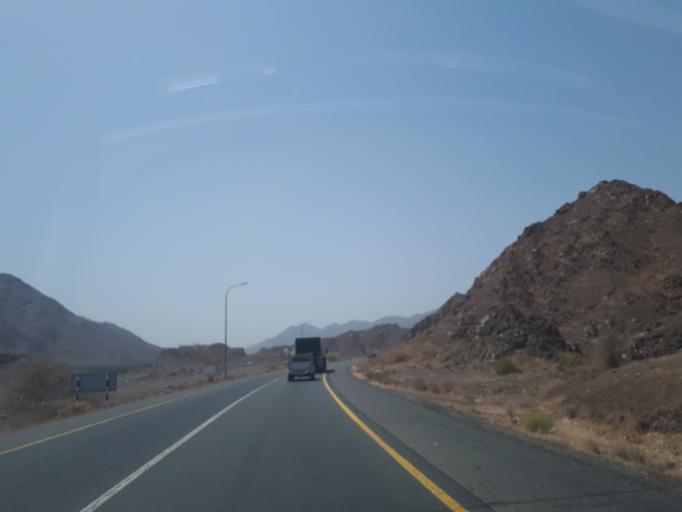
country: OM
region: Muhafazat ad Dakhiliyah
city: Sufalat Sama'il
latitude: 23.2166
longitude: 58.0762
